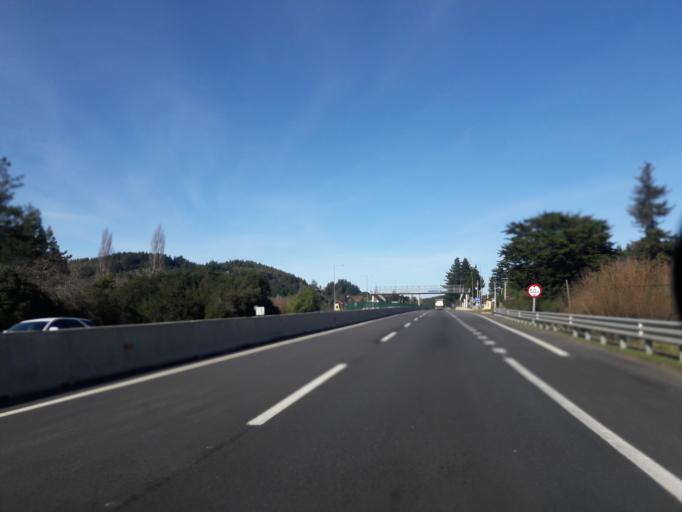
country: CL
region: Biobio
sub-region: Provincia de Biobio
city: Yumbel
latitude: -36.9492
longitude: -72.7504
